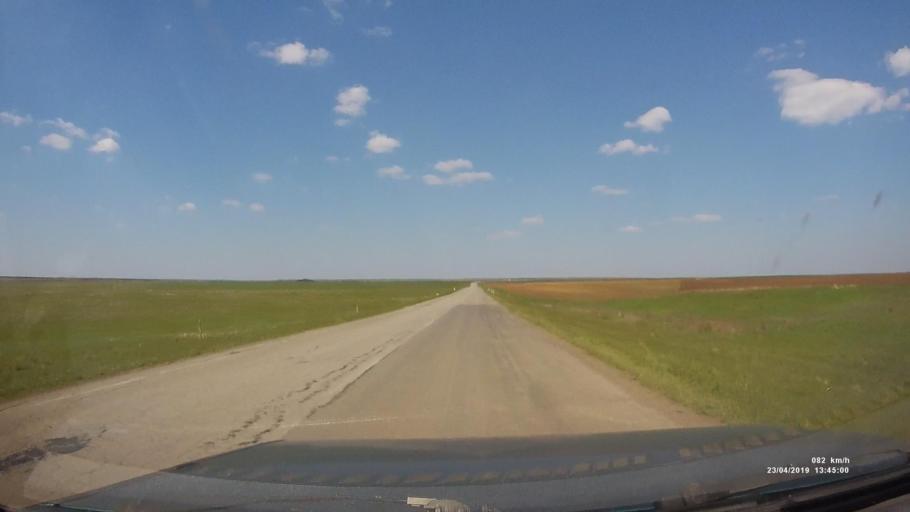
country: RU
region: Kalmykiya
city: Yashalta
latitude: 46.5874
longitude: 42.8195
